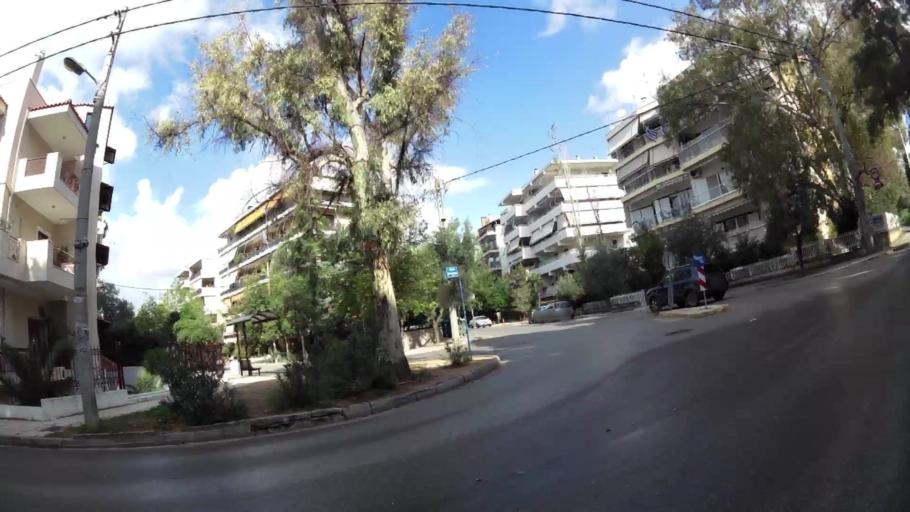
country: GR
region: Attica
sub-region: Nomarchia Athinas
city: Melissia
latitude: 38.0547
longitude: 23.8194
